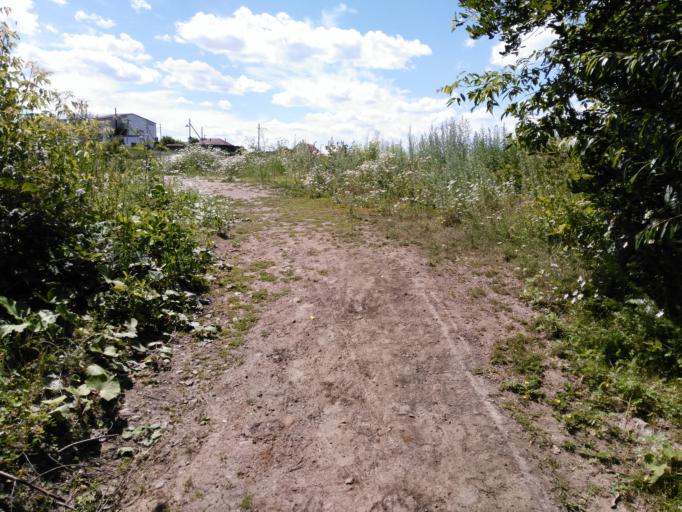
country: RU
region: Bashkortostan
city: Akhunovo
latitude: 54.2095
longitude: 59.5995
